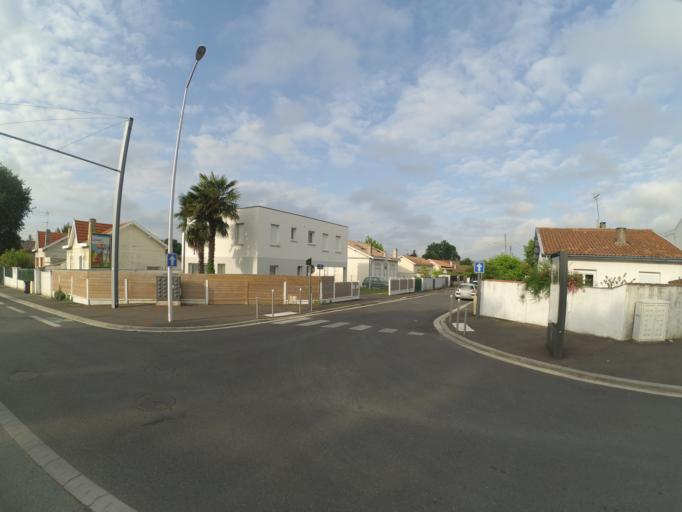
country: FR
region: Aquitaine
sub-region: Departement de la Gironde
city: Pessac
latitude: 44.7966
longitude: -0.6615
